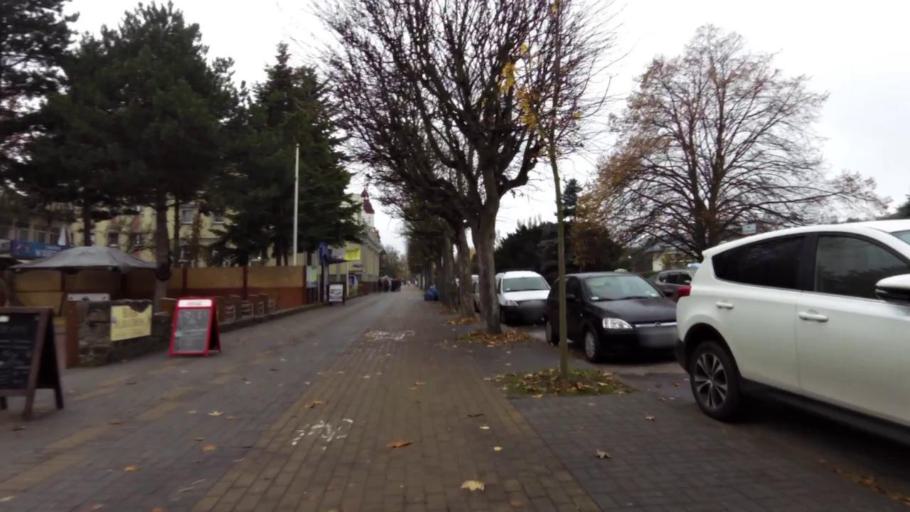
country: PL
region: West Pomeranian Voivodeship
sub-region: Swinoujscie
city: Swinoujscie
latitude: 53.9195
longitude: 14.2525
